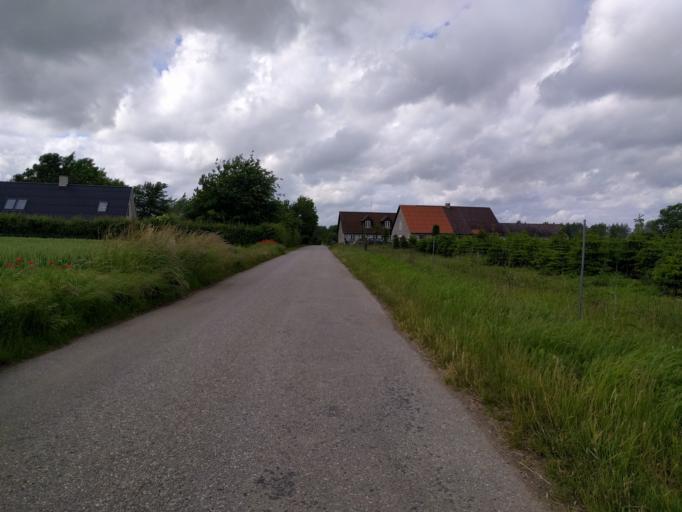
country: DK
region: South Denmark
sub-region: Odense Kommune
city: Bullerup
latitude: 55.4575
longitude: 10.5013
